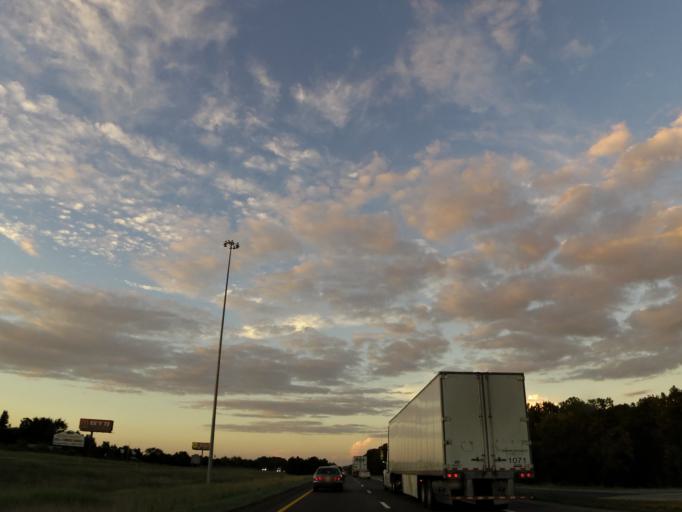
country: US
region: Tennessee
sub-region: Monroe County
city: Sweetwater
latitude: 35.6011
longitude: -84.5137
